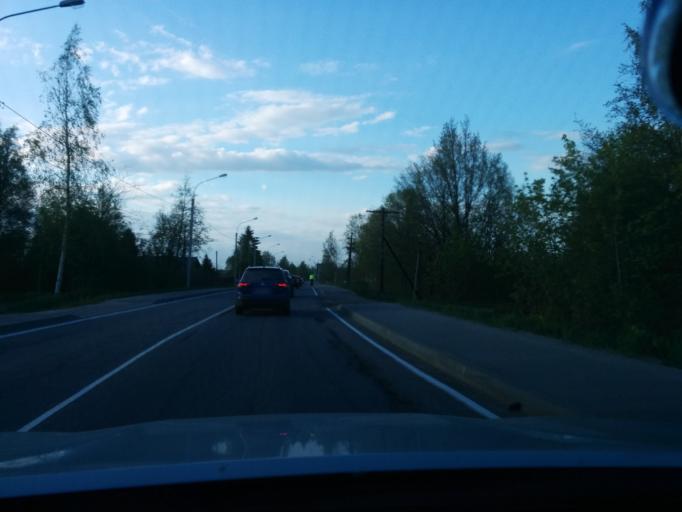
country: RU
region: Leningrad
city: Verkhniye Osel'ki
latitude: 60.2462
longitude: 30.4449
